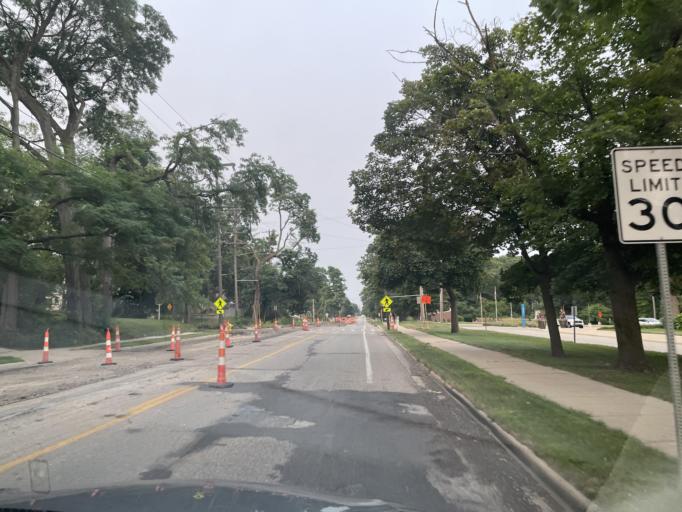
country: US
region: Michigan
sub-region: Kent County
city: East Grand Rapids
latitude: 42.9627
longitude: -85.6306
